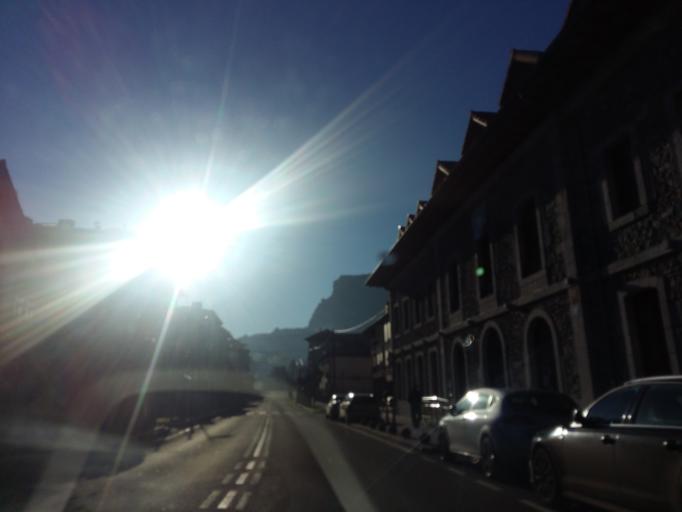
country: ES
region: Cantabria
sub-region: Provincia de Cantabria
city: Ramales de la Victoria
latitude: 43.2565
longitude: -3.4646
